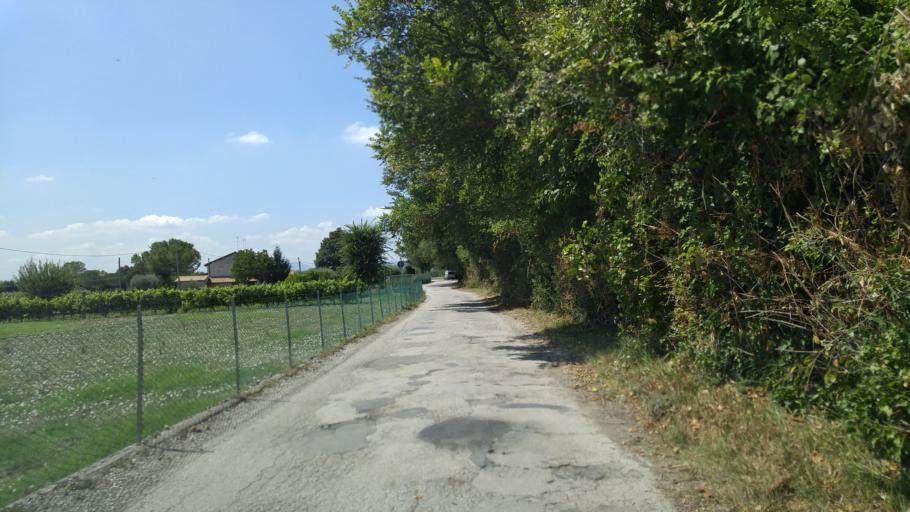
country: IT
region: The Marches
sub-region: Provincia di Pesaro e Urbino
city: Cuccurano
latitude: 43.7980
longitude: 12.9711
